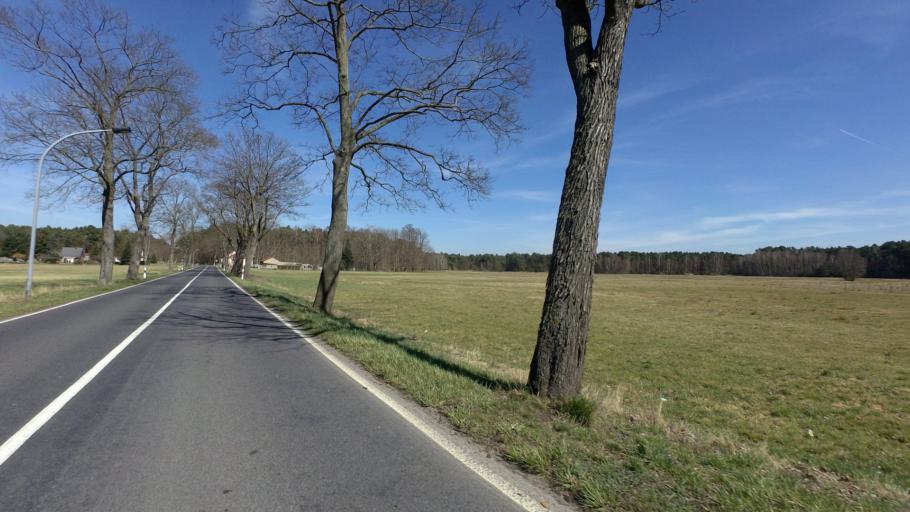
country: DE
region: Brandenburg
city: Storkow
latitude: 52.1958
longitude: 13.9207
